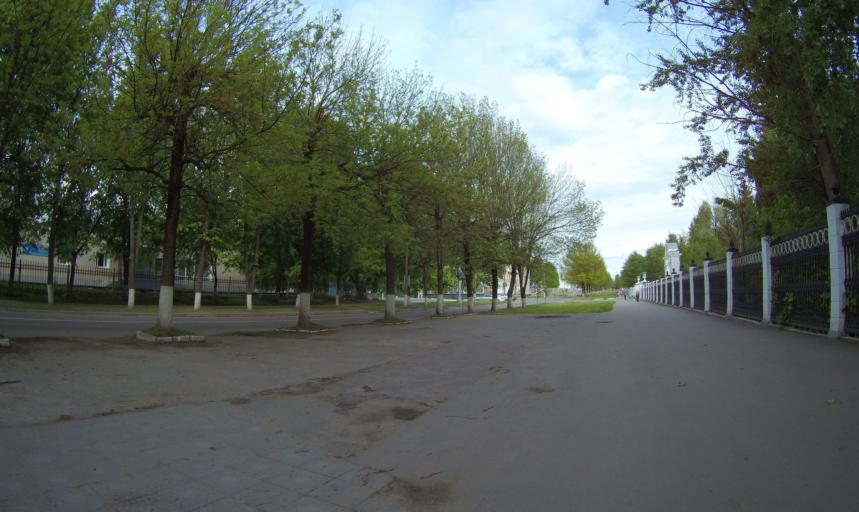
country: RU
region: Moskovskaya
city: Kolomna
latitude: 55.0885
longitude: 38.7774
